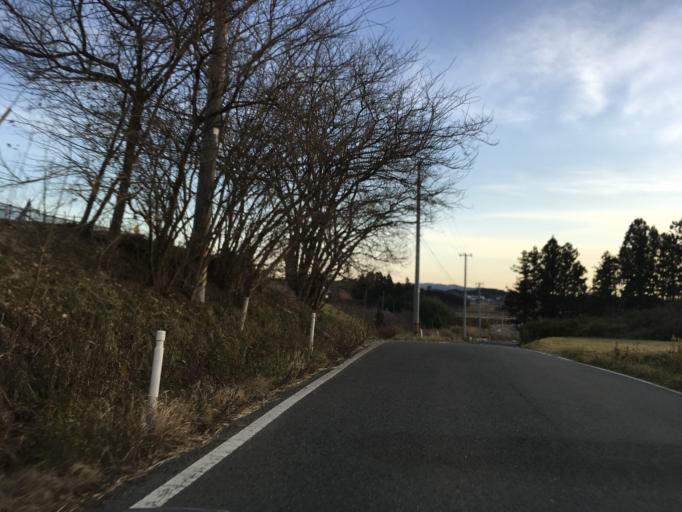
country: JP
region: Miyagi
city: Kogota
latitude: 38.6927
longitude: 141.0955
